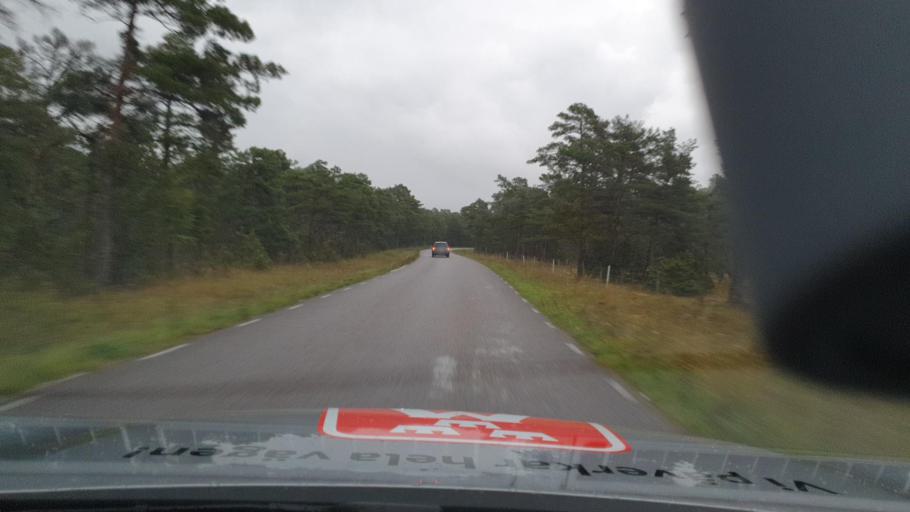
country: SE
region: Gotland
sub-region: Gotland
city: Slite
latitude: 57.7513
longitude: 18.7598
